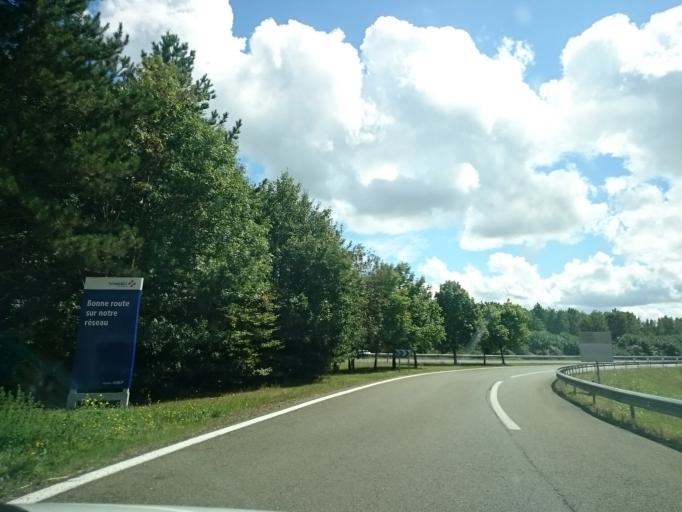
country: FR
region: Pays de la Loire
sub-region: Departement de la Sarthe
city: Parce-sur-Sarthe
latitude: 47.8068
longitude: -0.1689
